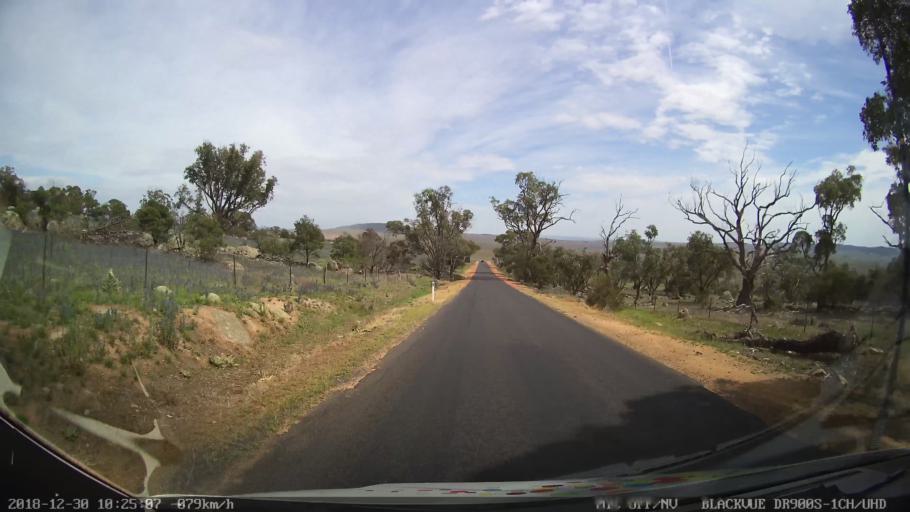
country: AU
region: New South Wales
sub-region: Snowy River
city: Berridale
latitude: -36.5284
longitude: 148.9614
